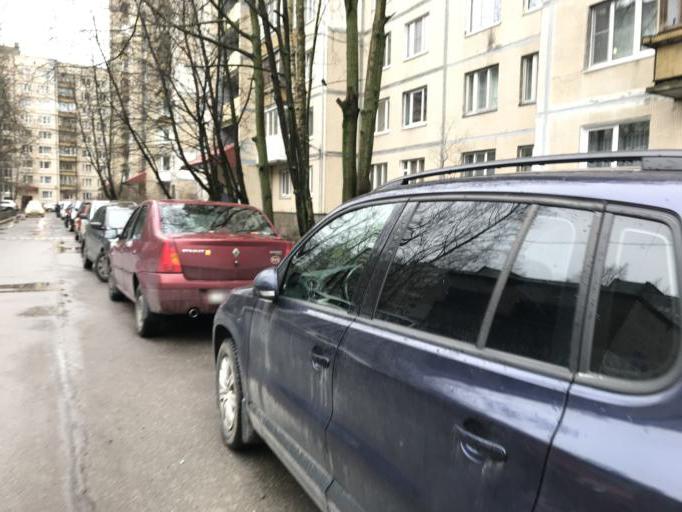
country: RU
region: St.-Petersburg
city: Ozerki
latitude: 60.0492
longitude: 30.3191
